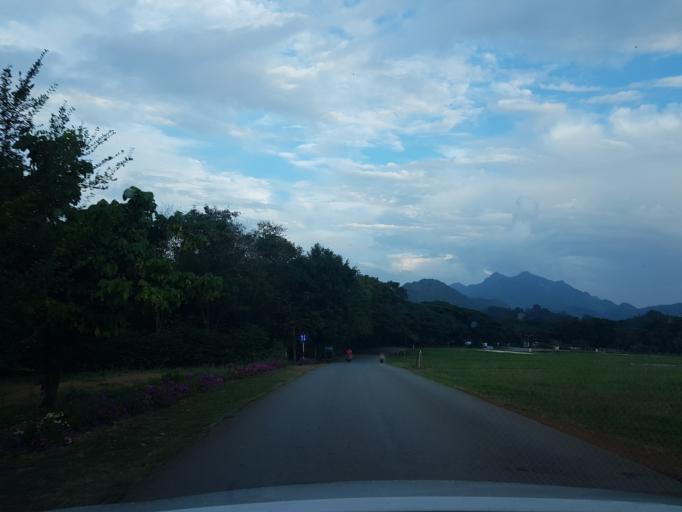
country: TH
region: Sara Buri
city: Muak Lek
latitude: 14.6327
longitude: 101.1931
